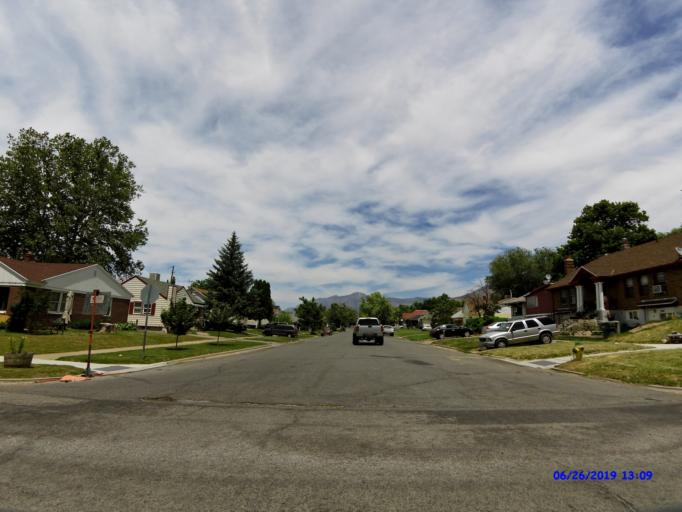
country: US
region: Utah
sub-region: Weber County
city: Ogden
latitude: 41.2122
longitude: -111.9624
